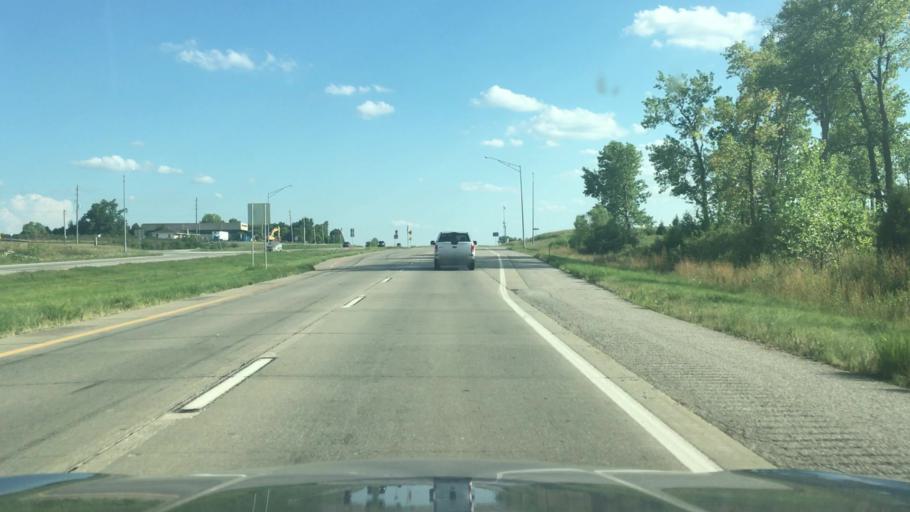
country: US
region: Missouri
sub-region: Jackson County
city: Lees Summit
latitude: 38.8794
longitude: -94.3741
